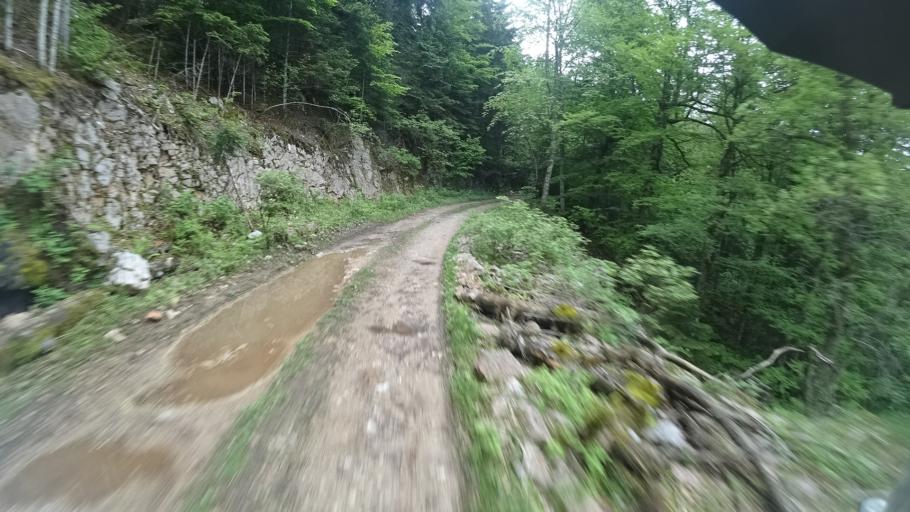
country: BA
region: Federation of Bosnia and Herzegovina
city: Bihac
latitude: 44.6336
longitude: 15.8184
